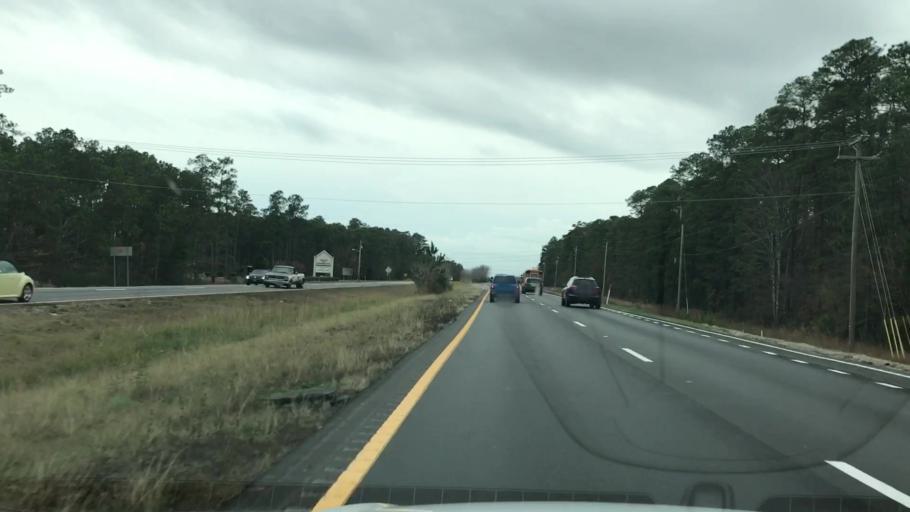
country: US
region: South Carolina
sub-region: Horry County
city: Garden City
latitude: 33.6120
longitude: -79.0111
